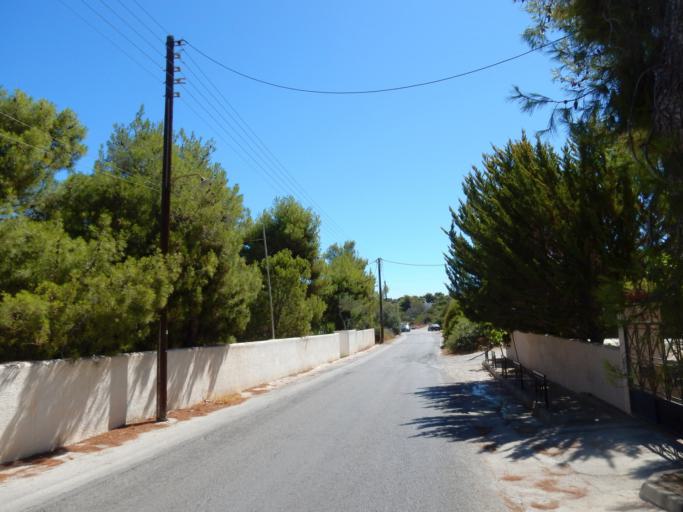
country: GR
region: Attica
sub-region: Nomos Piraios
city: Vathi
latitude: 37.7701
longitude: 23.4966
